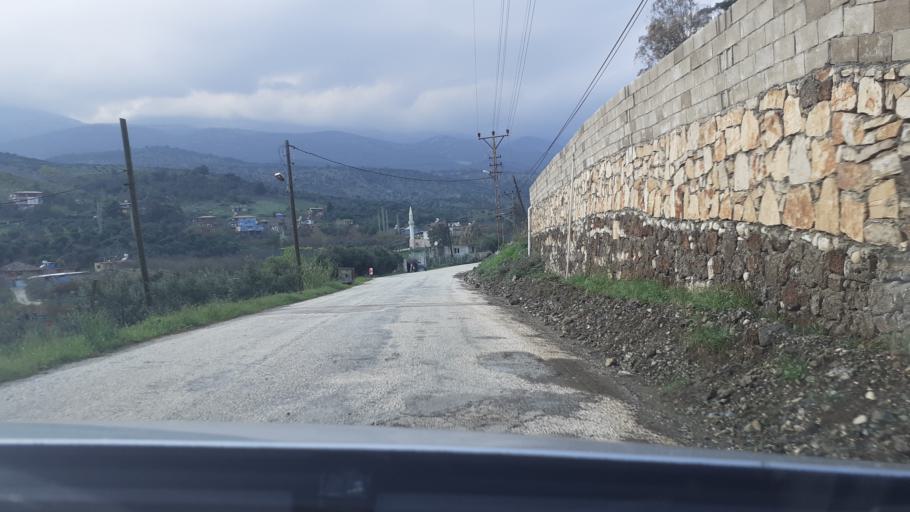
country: TR
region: Hatay
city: Kirikhan
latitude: 36.5031
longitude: 36.3246
